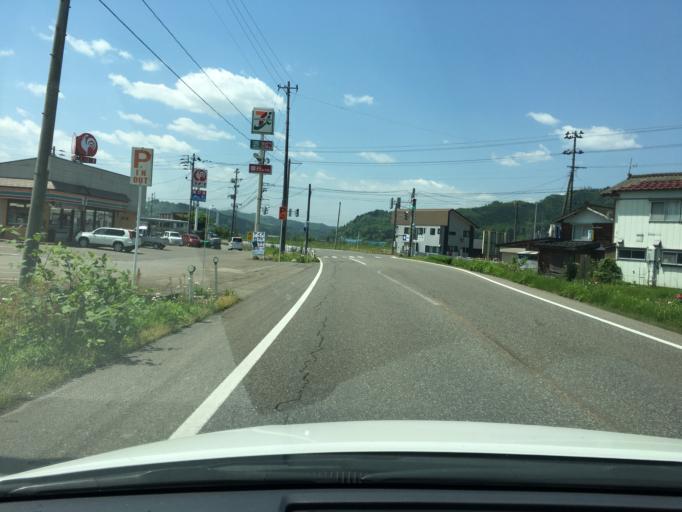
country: JP
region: Niigata
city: Ojiya
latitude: 37.2546
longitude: 138.9726
